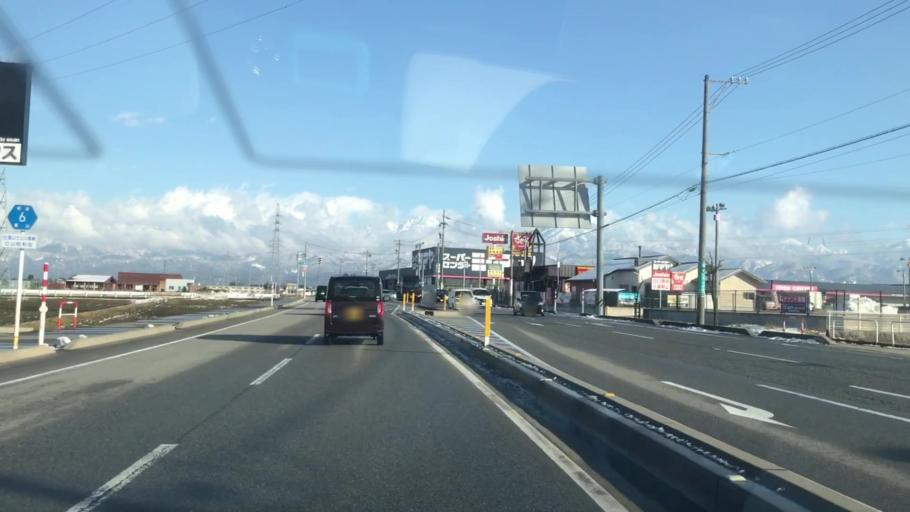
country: JP
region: Toyama
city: Kamiichi
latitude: 36.6863
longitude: 137.2924
